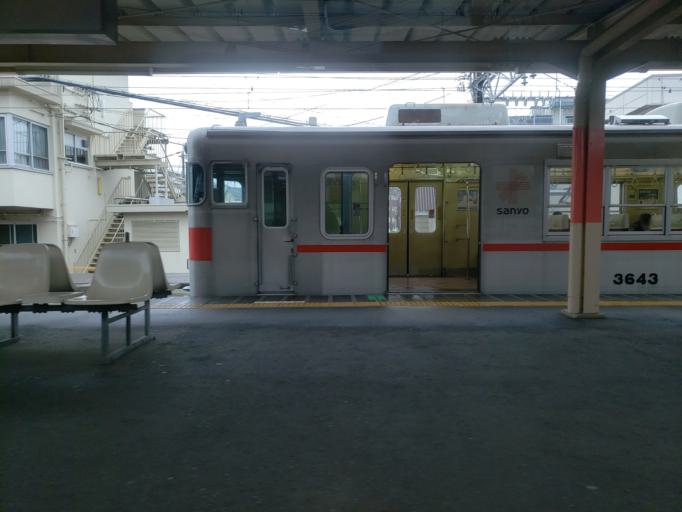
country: JP
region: Hyogo
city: Kakogawacho-honmachi
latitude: 34.7006
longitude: 134.8876
